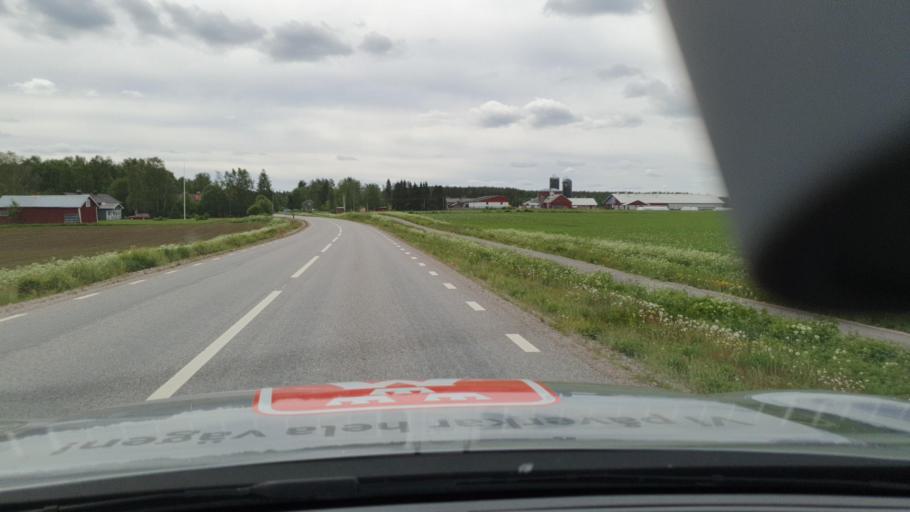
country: SE
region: Norrbotten
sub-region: Kalix Kommun
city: Kalix
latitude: 65.9241
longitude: 23.4604
